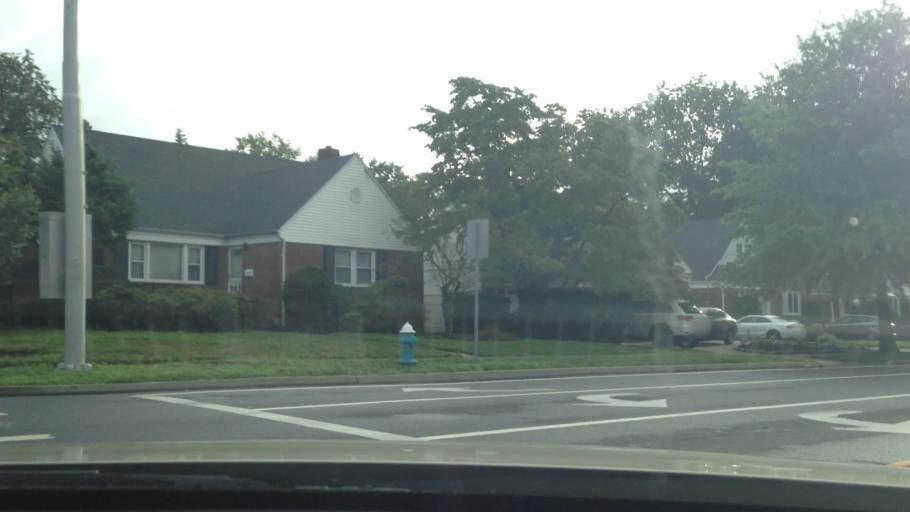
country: US
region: New York
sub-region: Nassau County
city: Stewart Manor
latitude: 40.7248
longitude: -73.6874
